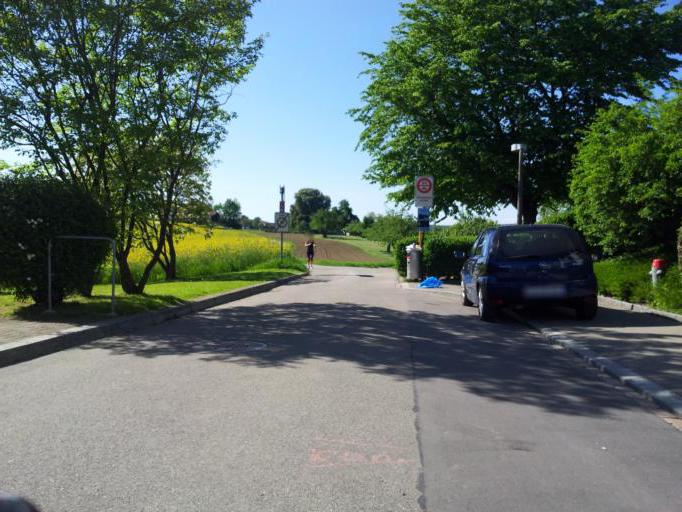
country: CH
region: Zurich
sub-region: Bezirk Dietikon
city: Schlieren / Boden
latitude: 47.3904
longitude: 8.4677
